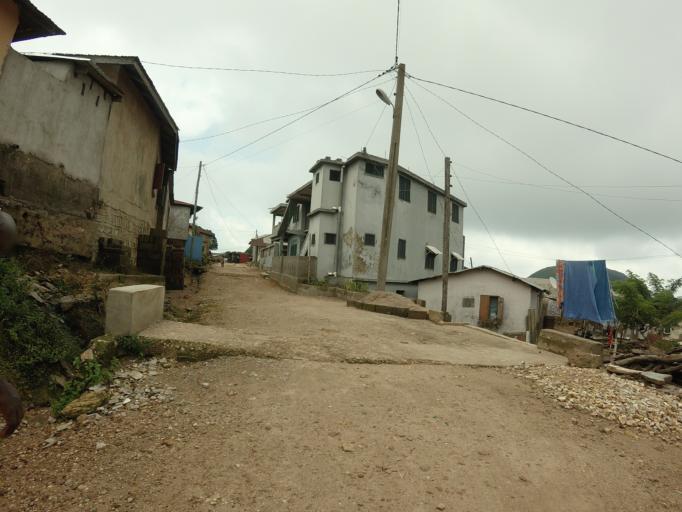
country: TG
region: Plateaux
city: Kpalime
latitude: 6.8472
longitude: 0.4366
